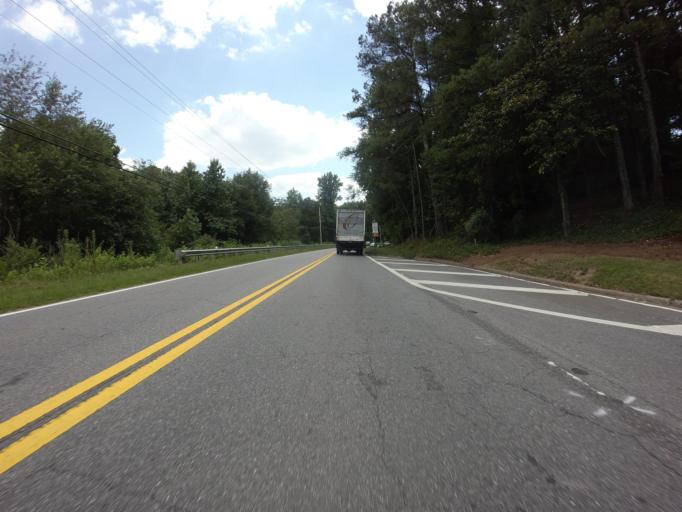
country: US
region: Georgia
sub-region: Gwinnett County
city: Norcross
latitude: 33.9909
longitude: -84.2593
